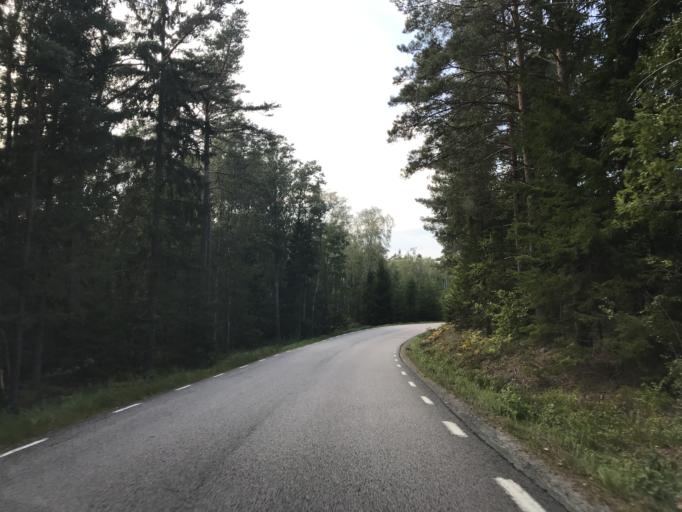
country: SE
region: Stockholm
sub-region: Norrtalje Kommun
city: Bjorko
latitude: 59.8818
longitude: 18.9812
